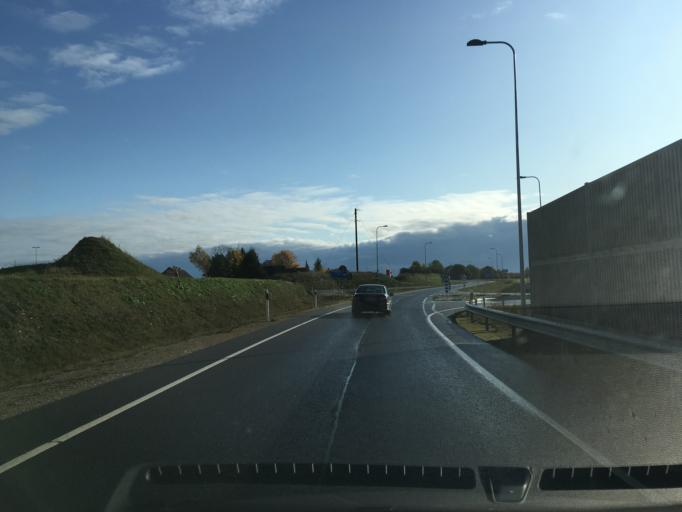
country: EE
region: Harju
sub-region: Rae vald
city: Vaida
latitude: 59.1829
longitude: 25.1101
